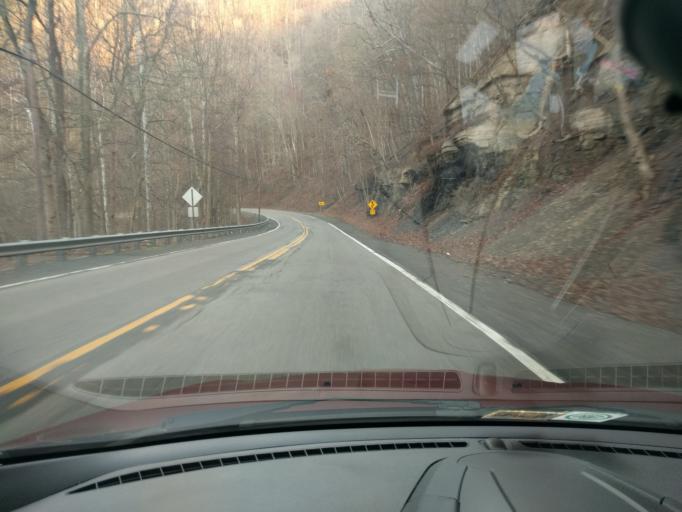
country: US
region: West Virginia
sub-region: Fayette County
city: Ansted
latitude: 38.1432
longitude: -81.1550
